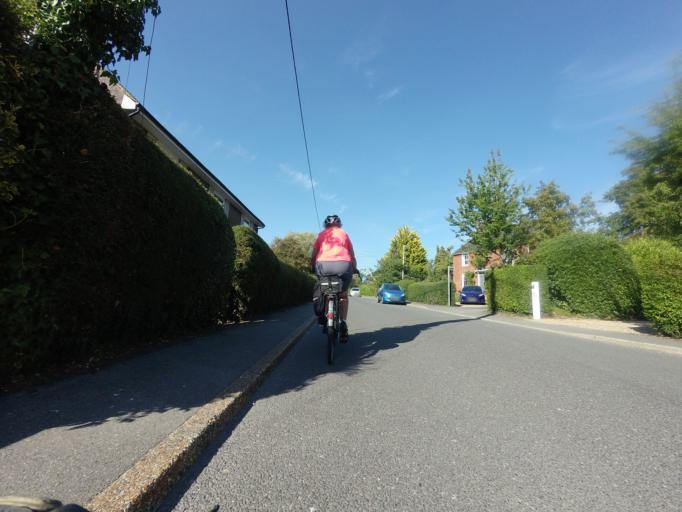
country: GB
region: England
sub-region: Kent
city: Tenterden
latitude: 51.0128
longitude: 0.7072
